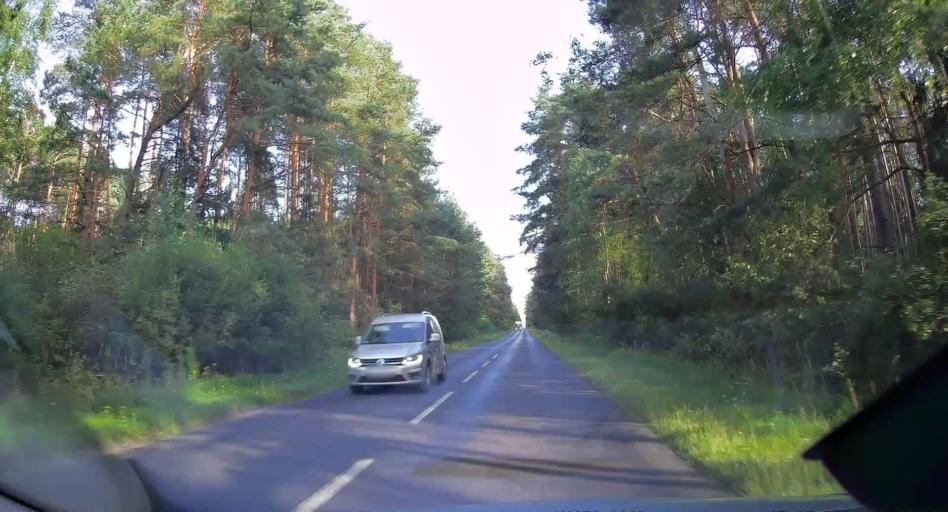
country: PL
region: Swietokrzyskie
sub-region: Powiat konecki
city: Smykow
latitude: 51.0969
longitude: 20.3610
